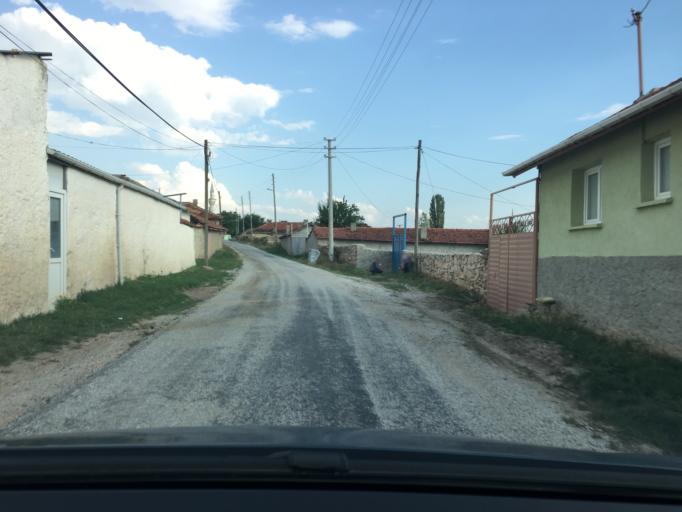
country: TR
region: Eskisehir
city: Kirka
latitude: 39.2781
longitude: 30.6752
